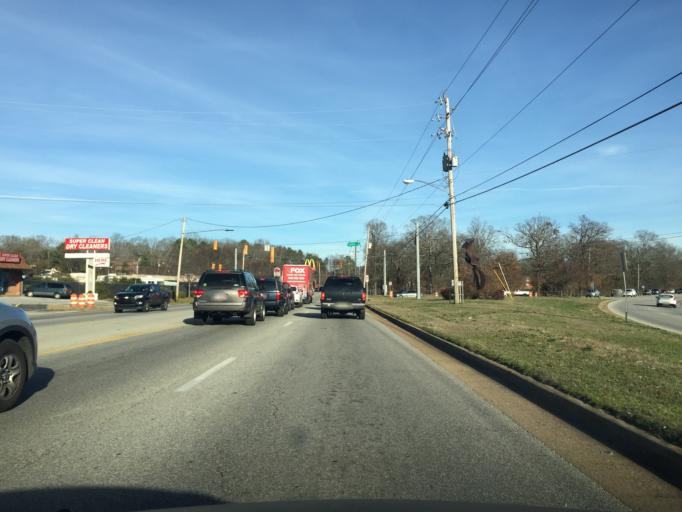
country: US
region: Tennessee
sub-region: Hamilton County
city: Red Bank
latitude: 35.1142
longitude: -85.2578
